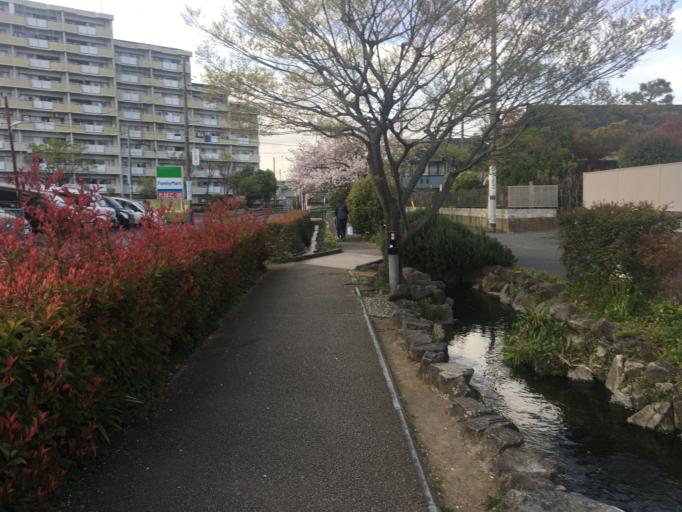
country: JP
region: Kanagawa
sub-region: Kawasaki-shi
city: Kawasaki
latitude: 35.5790
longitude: 139.6296
